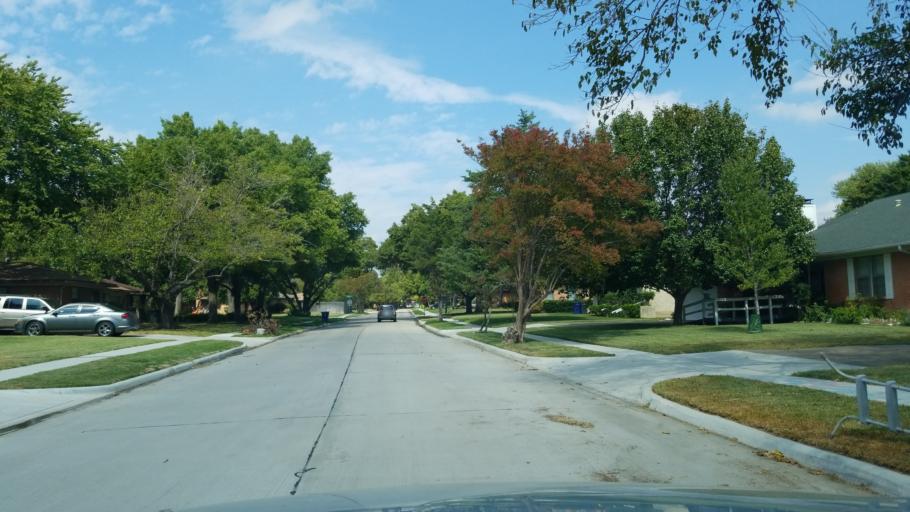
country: US
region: Texas
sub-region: Dallas County
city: Garland
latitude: 32.8953
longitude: -96.6578
